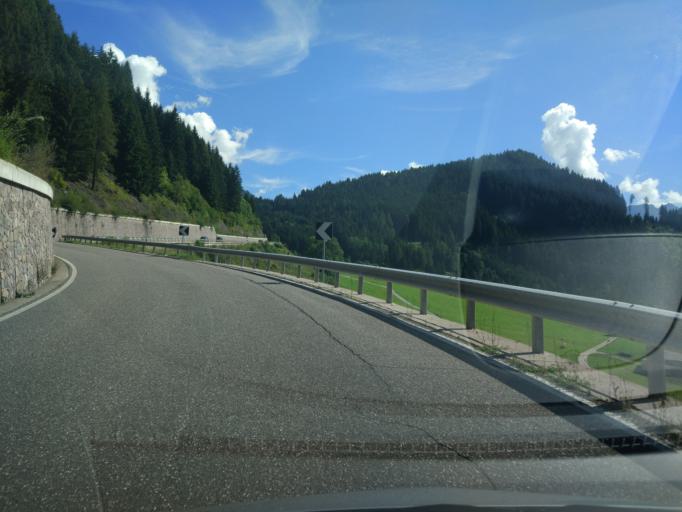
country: IT
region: Trentino-Alto Adige
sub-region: Provincia di Trento
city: Predazzo
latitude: 46.3123
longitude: 11.6375
